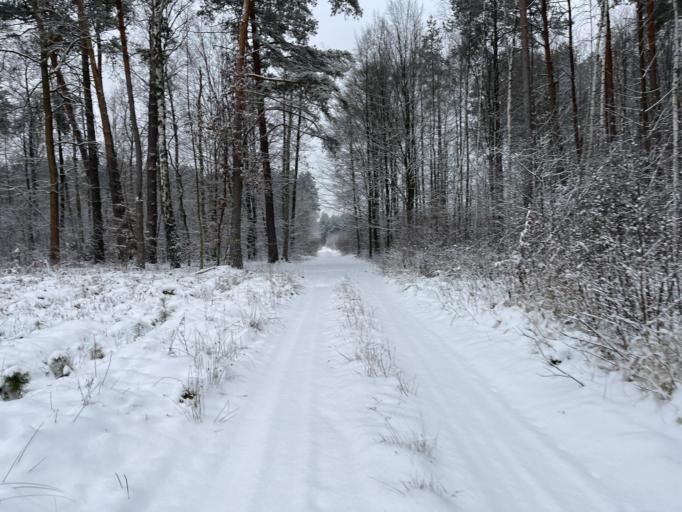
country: PL
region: Masovian Voivodeship
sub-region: Powiat zyrardowski
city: Mrozy
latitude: 52.0357
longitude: 20.2716
